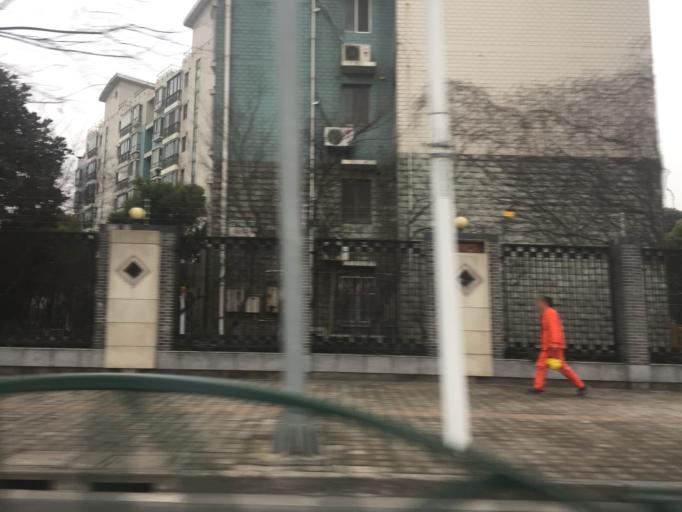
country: CN
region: Shanghai Shi
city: Luwan
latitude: 31.1875
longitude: 121.4953
